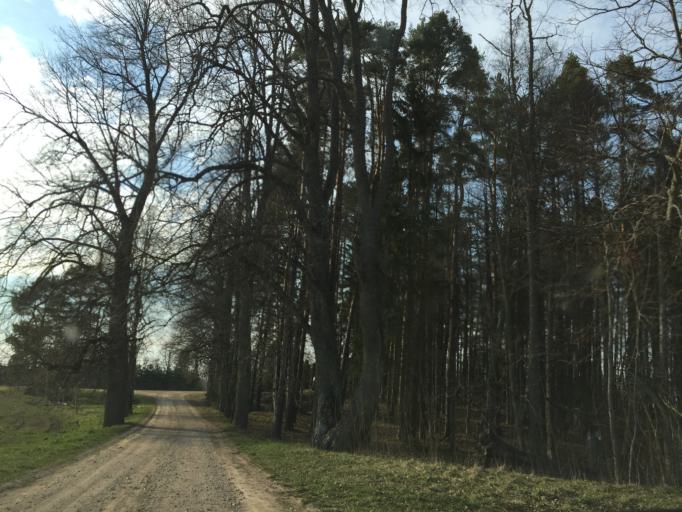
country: EE
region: Jogevamaa
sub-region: Mustvee linn
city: Mustvee
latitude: 58.8609
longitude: 26.8396
